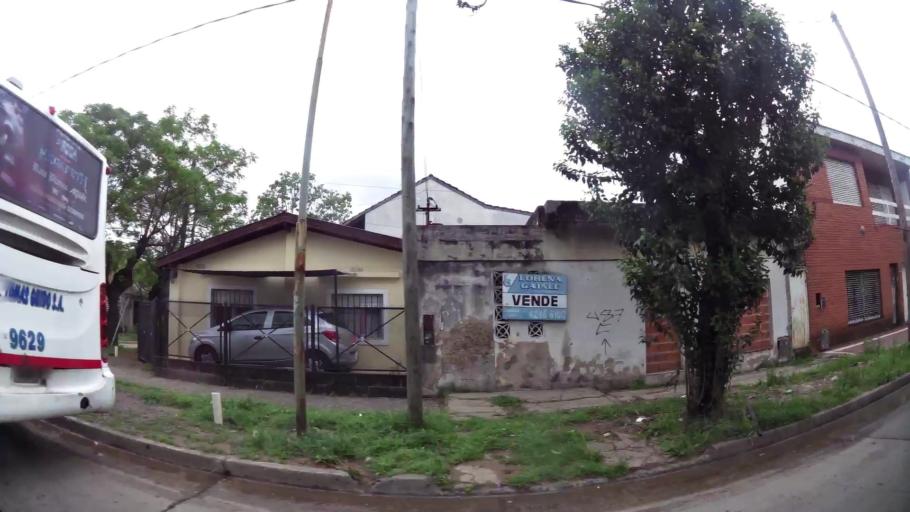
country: AR
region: Buenos Aires
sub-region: Partido de Lanus
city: Lanus
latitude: -34.7261
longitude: -58.3835
